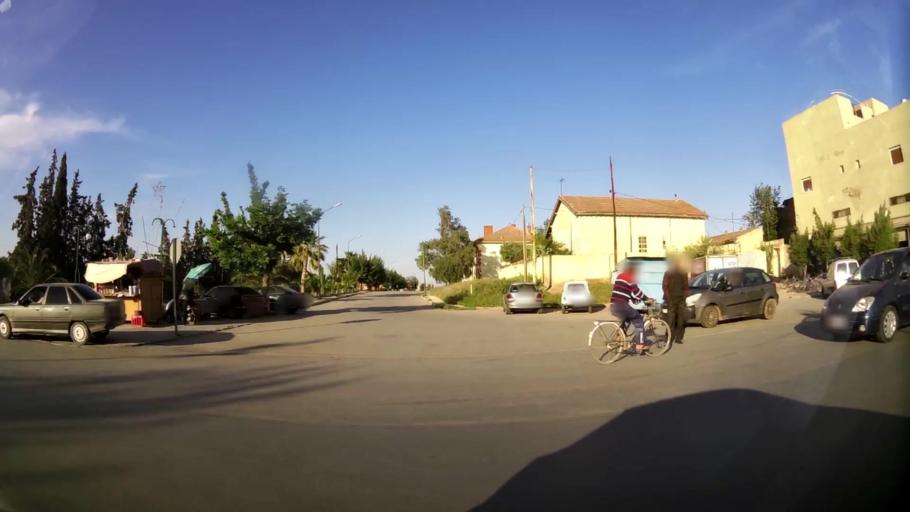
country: MA
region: Oriental
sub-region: Oujda-Angad
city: Oujda
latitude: 34.6980
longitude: -1.9100
